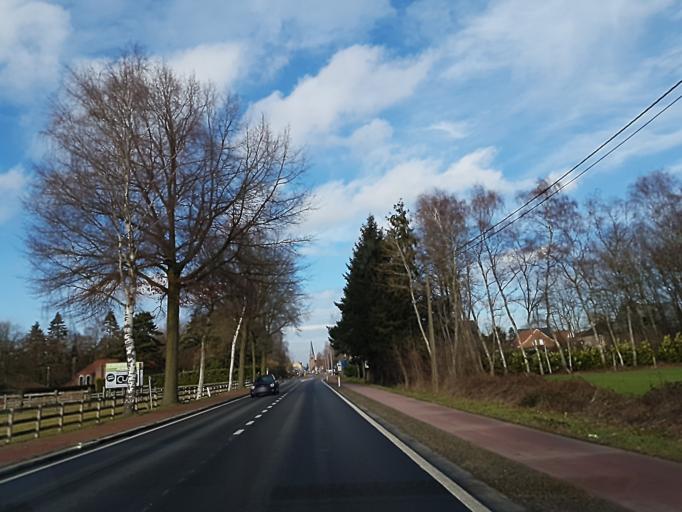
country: BE
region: Flanders
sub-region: Provincie Antwerpen
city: Dessel
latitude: 51.2326
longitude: 5.1139
